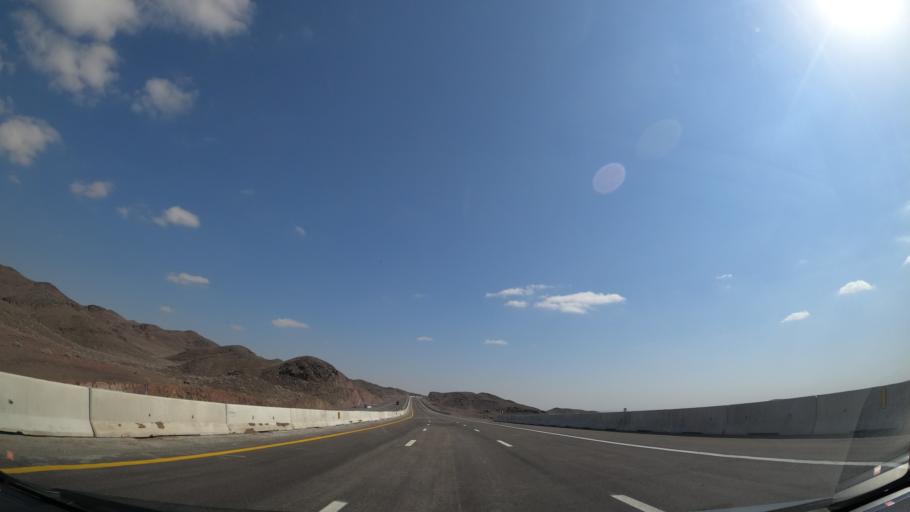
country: IR
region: Alborz
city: Eshtehard
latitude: 35.6636
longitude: 50.6508
